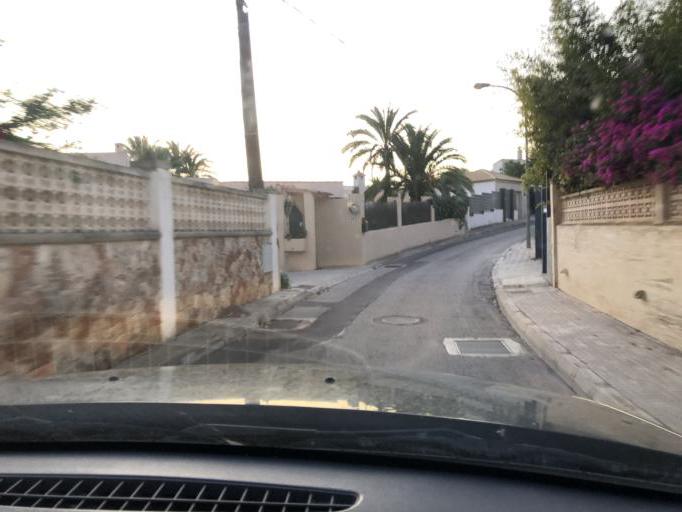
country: ES
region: Balearic Islands
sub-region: Illes Balears
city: Santa Ponsa
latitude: 39.5251
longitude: 2.4842
